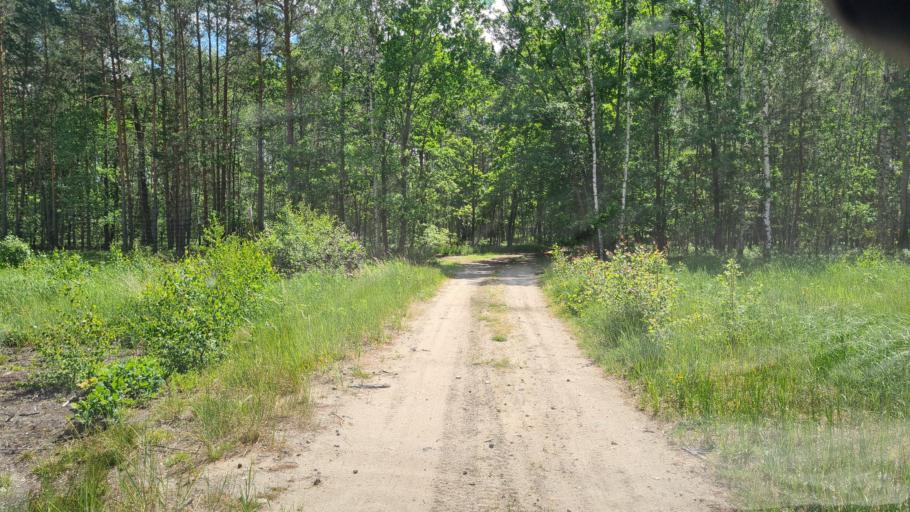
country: DE
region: Brandenburg
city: Sallgast
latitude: 51.5981
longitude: 13.8150
